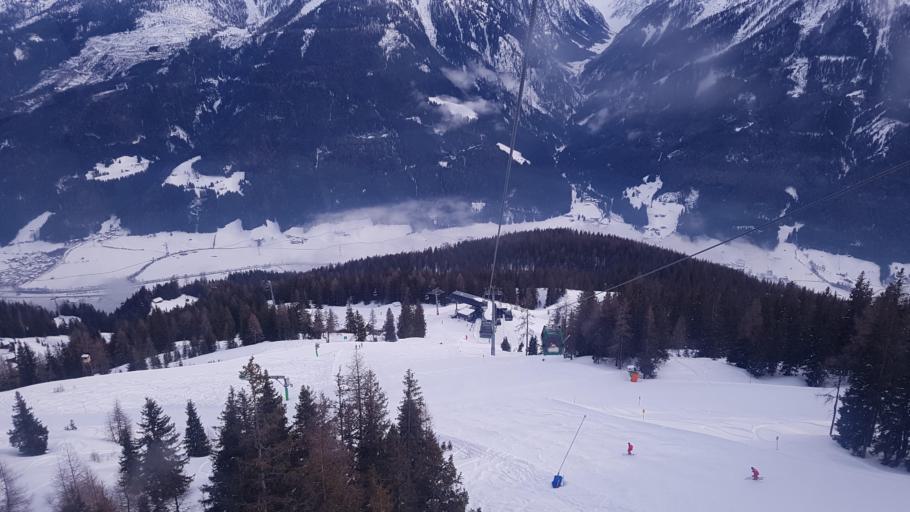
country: AT
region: Salzburg
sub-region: Politischer Bezirk Zell am See
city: Neukirchen am Grossvenediger
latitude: 47.2751
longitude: 12.3009
